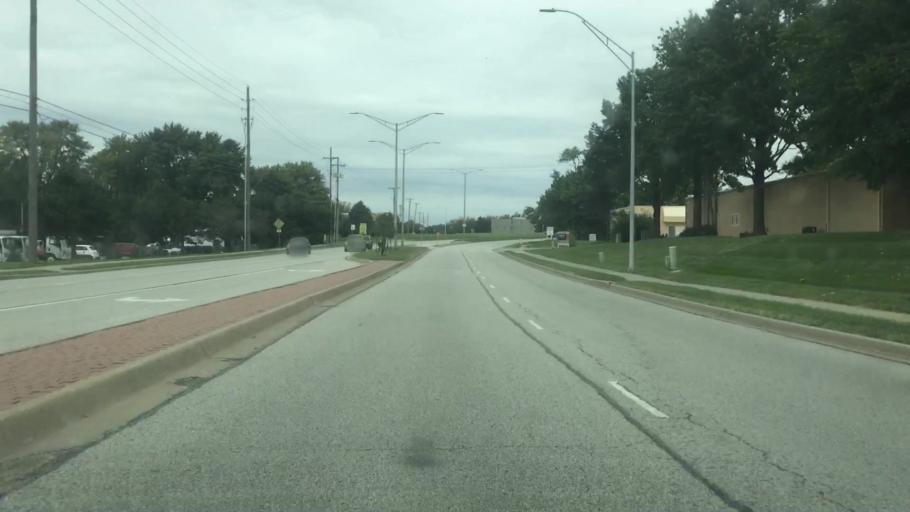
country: US
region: Kansas
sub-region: Johnson County
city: Lenexa
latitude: 38.9188
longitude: -94.7609
